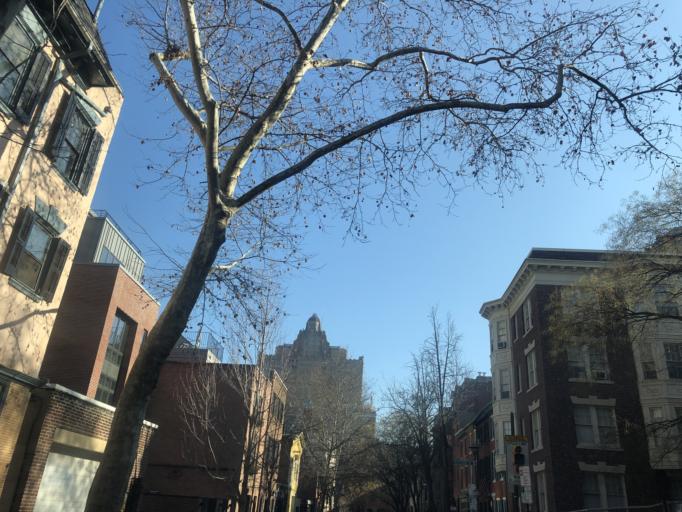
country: US
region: Pennsylvania
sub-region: Philadelphia County
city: Philadelphia
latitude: 39.9471
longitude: -75.1713
